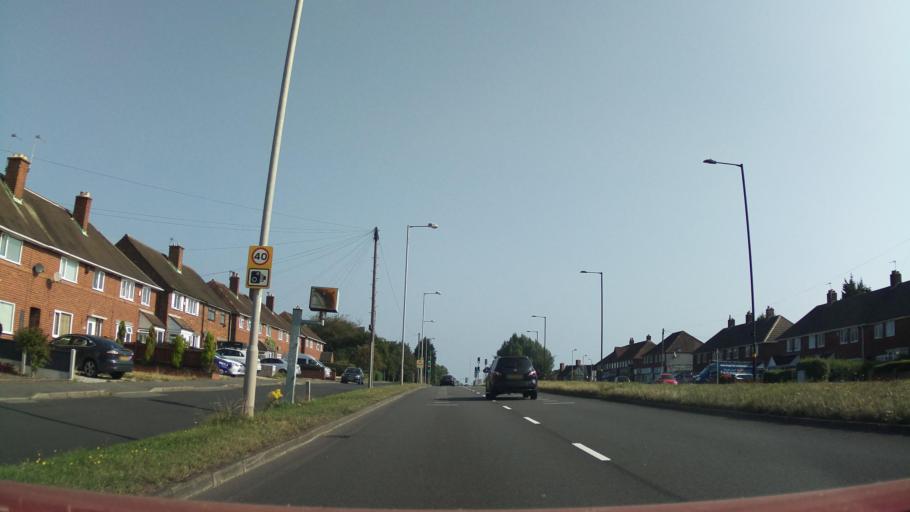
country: GB
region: England
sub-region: Walsall
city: Streetly
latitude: 52.5600
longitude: -1.8953
